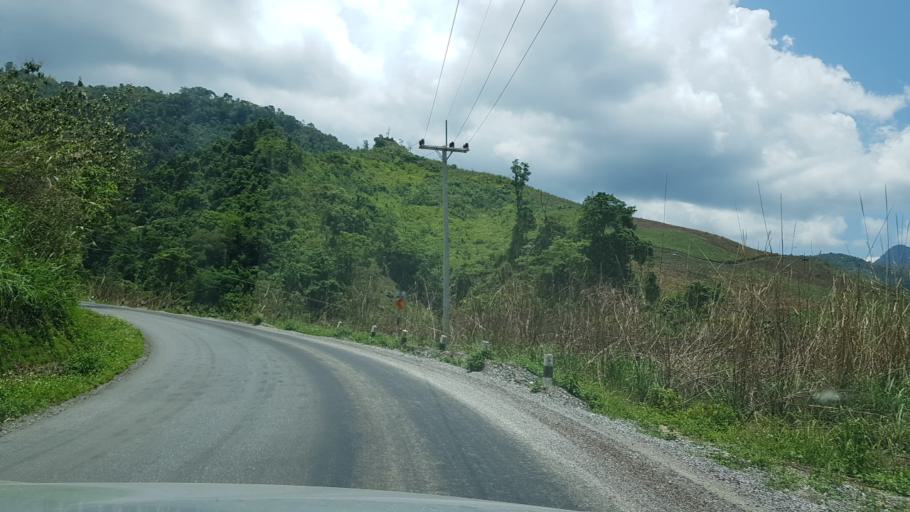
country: LA
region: Vientiane
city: Muang Kasi
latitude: 19.1395
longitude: 102.2918
